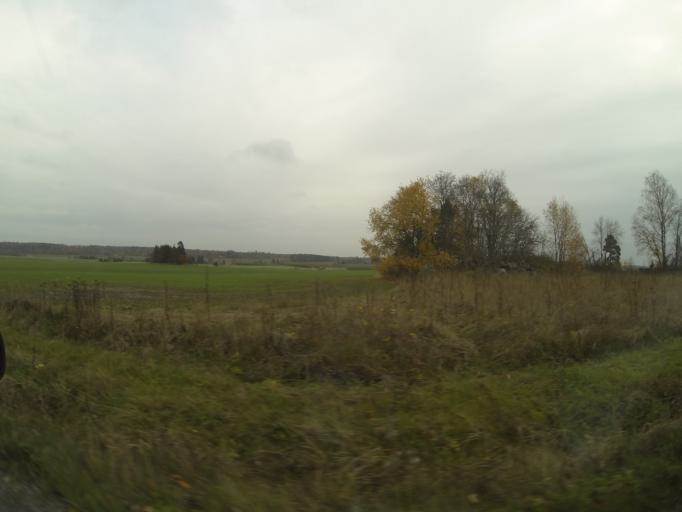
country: SE
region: Vaestmanland
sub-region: Vasteras
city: Skultuna
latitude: 59.6618
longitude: 16.4604
